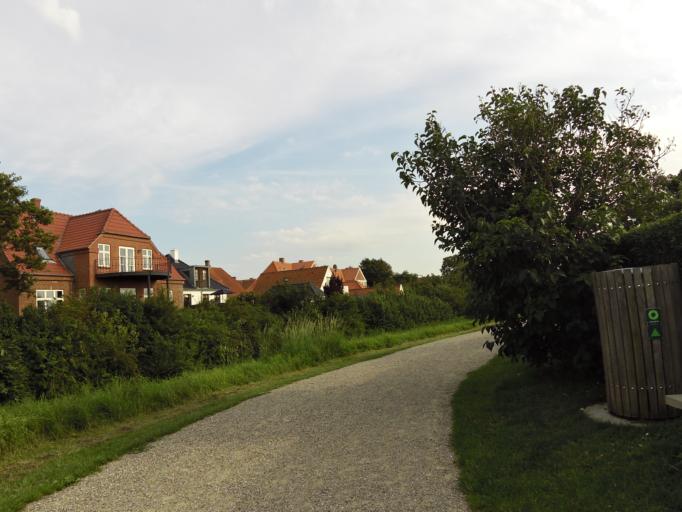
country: DK
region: South Denmark
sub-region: Esbjerg Kommune
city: Ribe
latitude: 55.3299
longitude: 8.7556
